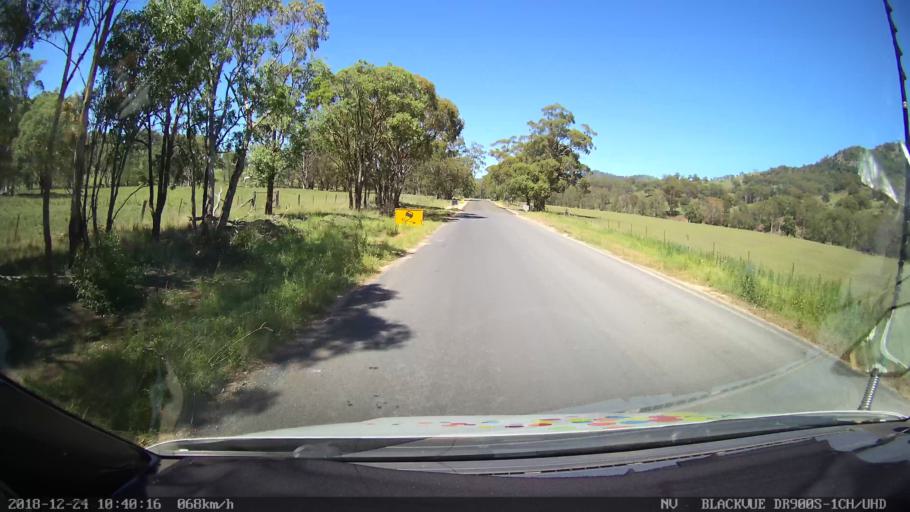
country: AU
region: New South Wales
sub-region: Upper Hunter Shire
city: Merriwa
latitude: -31.8606
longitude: 150.4689
